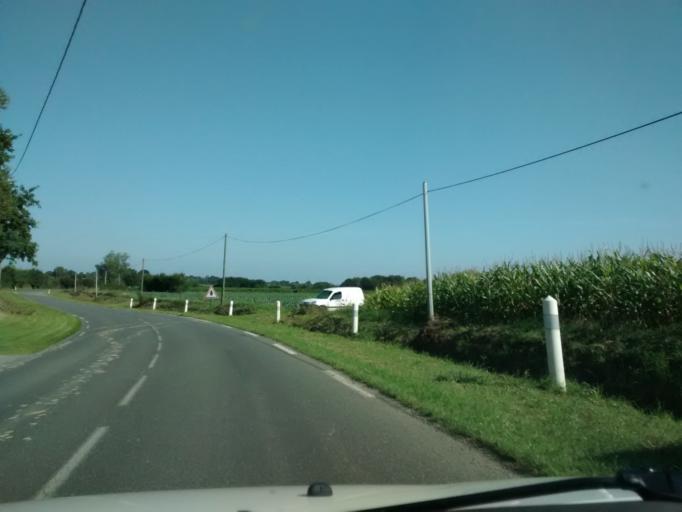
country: FR
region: Brittany
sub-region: Departement des Cotes-d'Armor
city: Tredarzec
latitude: 48.8169
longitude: -3.1896
